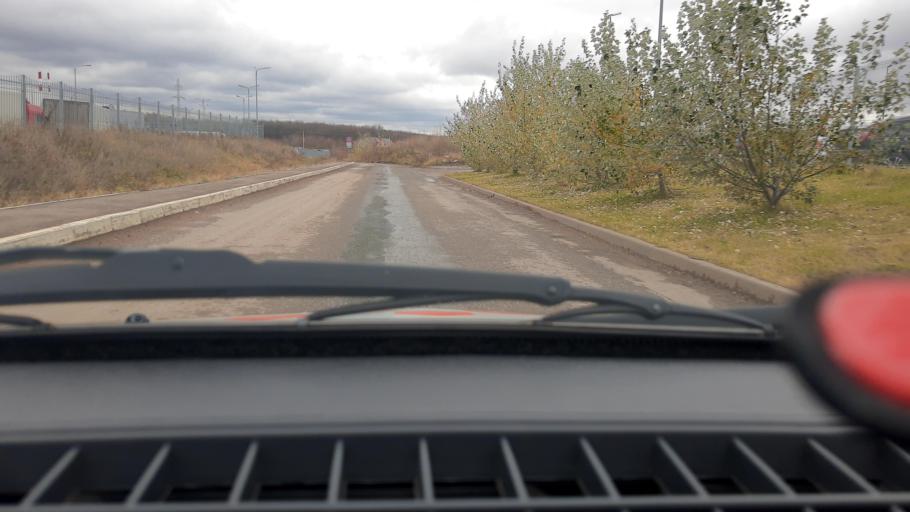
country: RU
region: Bashkortostan
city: Ufa
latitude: 54.6684
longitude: 55.9293
